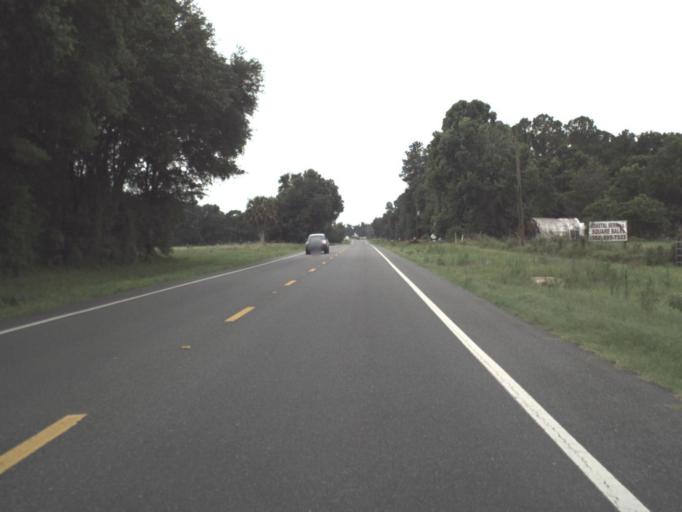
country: US
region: Florida
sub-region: Levy County
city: Williston
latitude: 29.3444
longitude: -82.4558
